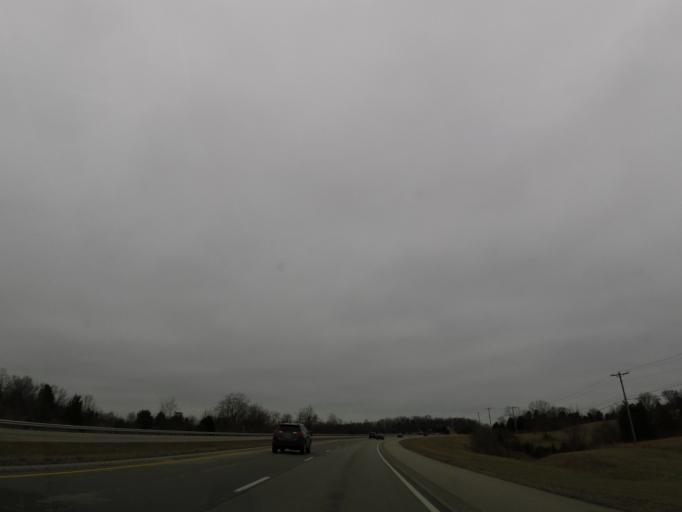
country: US
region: Kentucky
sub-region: Franklin County
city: Frankfort
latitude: 38.1404
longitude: -84.9029
